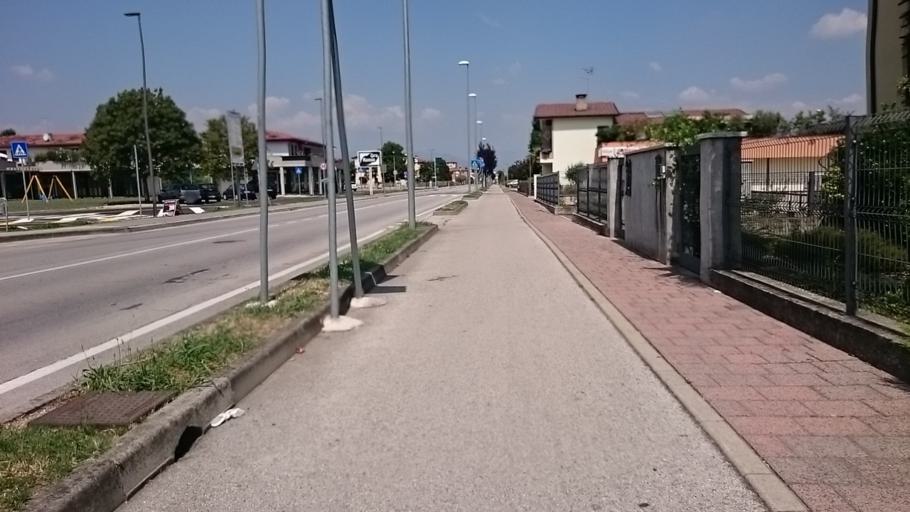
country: IT
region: Veneto
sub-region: Provincia di Padova
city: Cittadella
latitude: 45.6320
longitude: 11.7905
